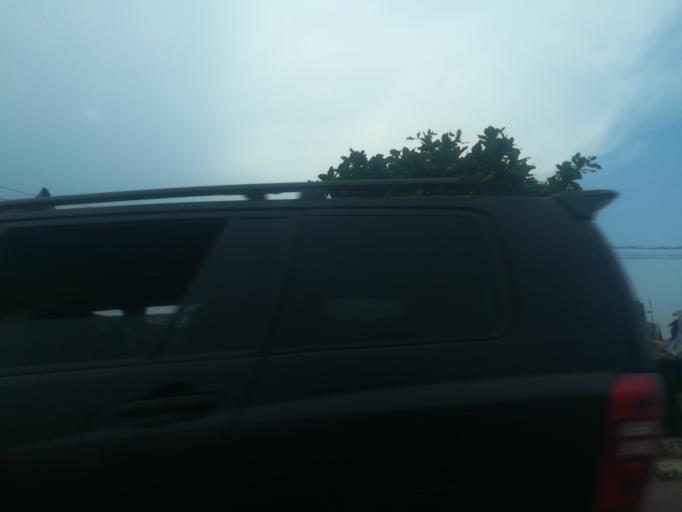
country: NG
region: Oyo
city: Ibadan
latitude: 7.3677
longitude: 3.8283
